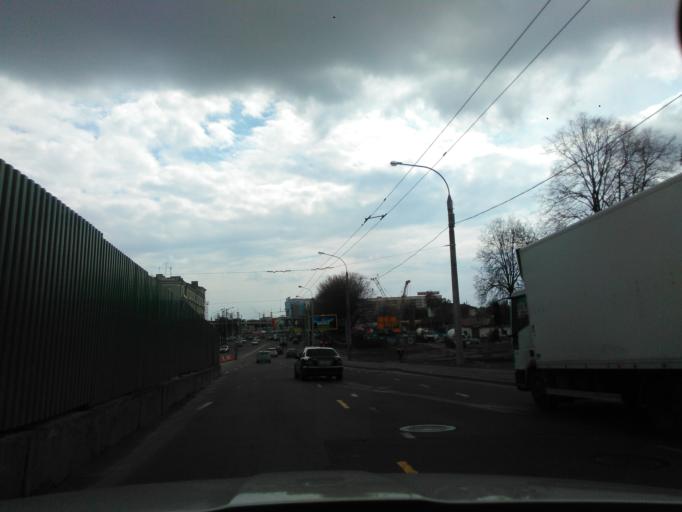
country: BY
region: Minsk
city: Minsk
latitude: 53.8953
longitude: 27.5388
